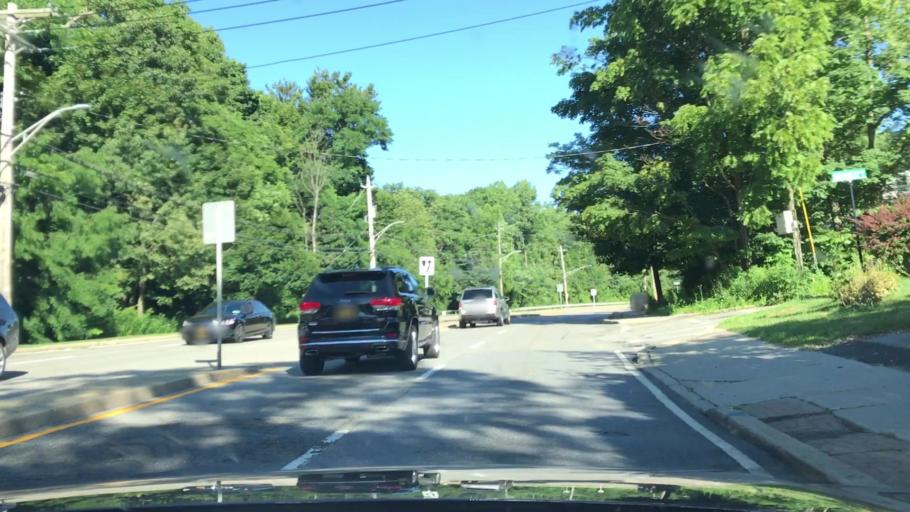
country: US
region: New York
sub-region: Westchester County
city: Thornwood
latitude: 41.1233
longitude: -73.7779
